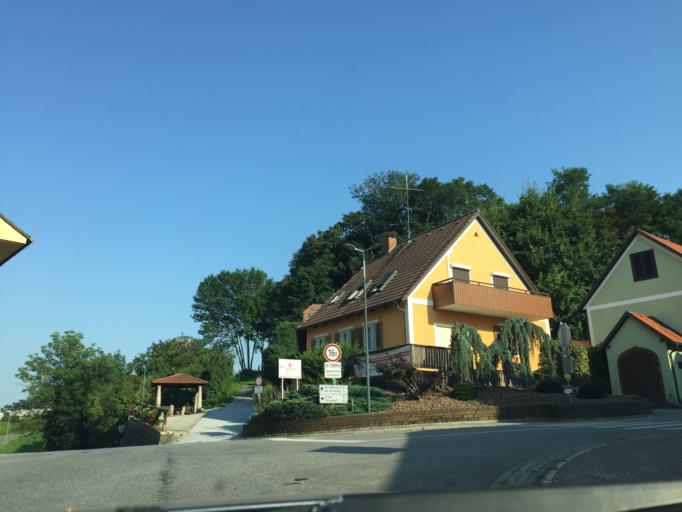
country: AT
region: Styria
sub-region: Politischer Bezirk Suedoststeiermark
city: Straden
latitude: 46.8075
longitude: 15.8691
